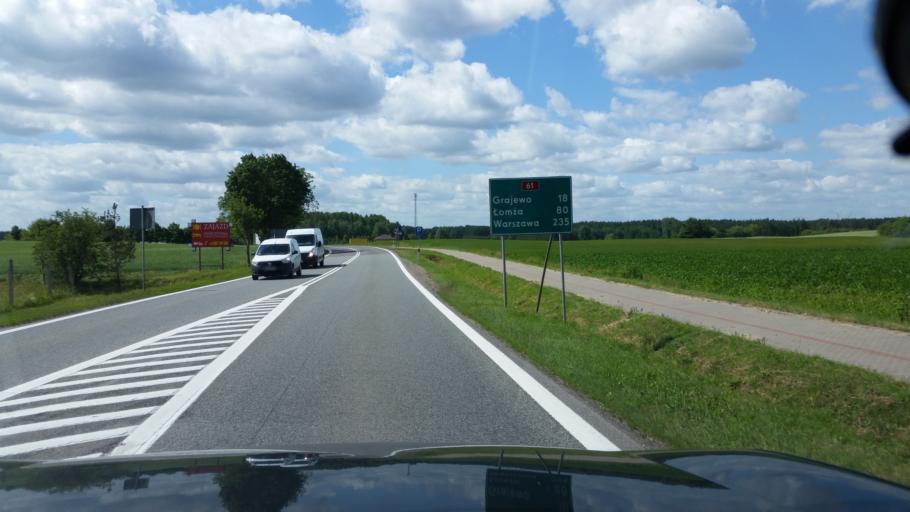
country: PL
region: Podlasie
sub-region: Powiat grajewski
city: Rajgrod
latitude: 53.7238
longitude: 22.6774
